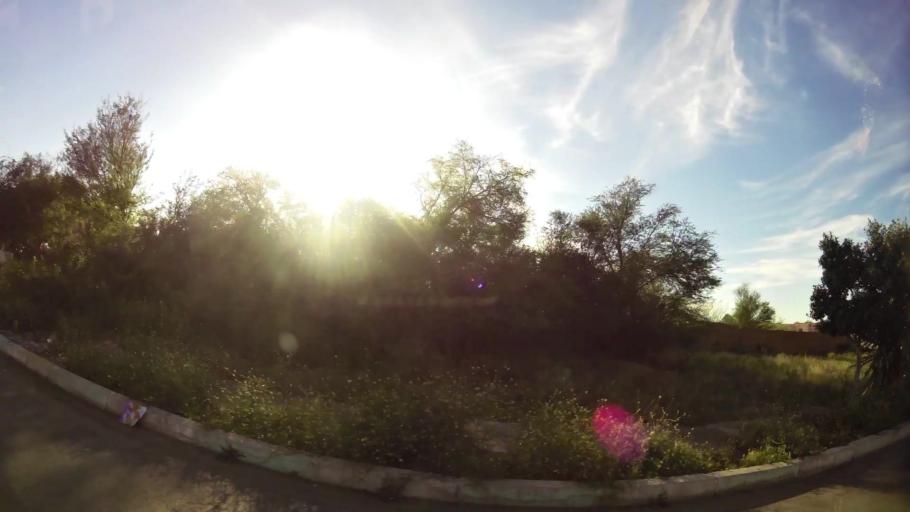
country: MA
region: Marrakech-Tensift-Al Haouz
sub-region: Marrakech
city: Marrakesh
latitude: 31.6795
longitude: -8.0644
